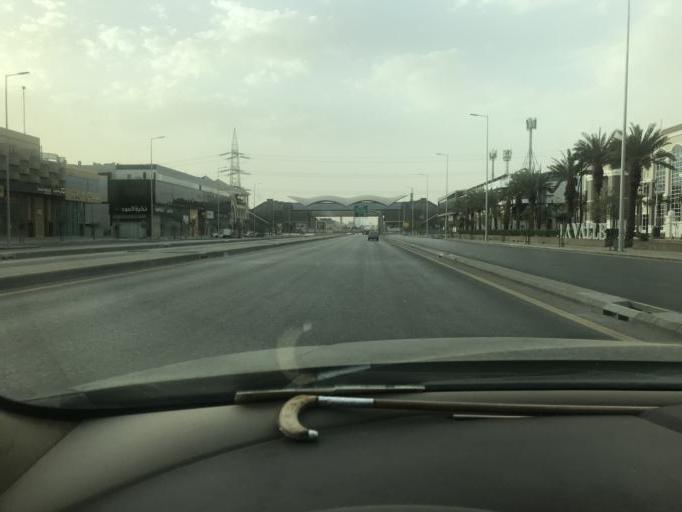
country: SA
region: Ar Riyad
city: Riyadh
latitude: 24.7830
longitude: 46.6620
